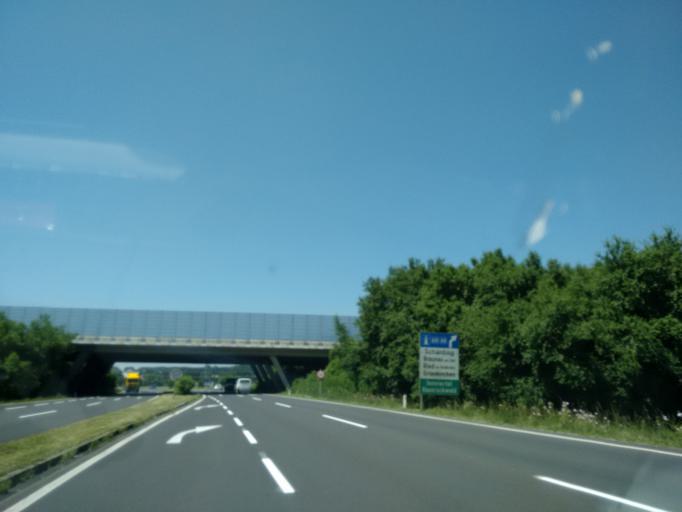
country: AT
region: Upper Austria
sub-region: Wels Stadt
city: Wels
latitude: 48.1854
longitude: 14.0231
